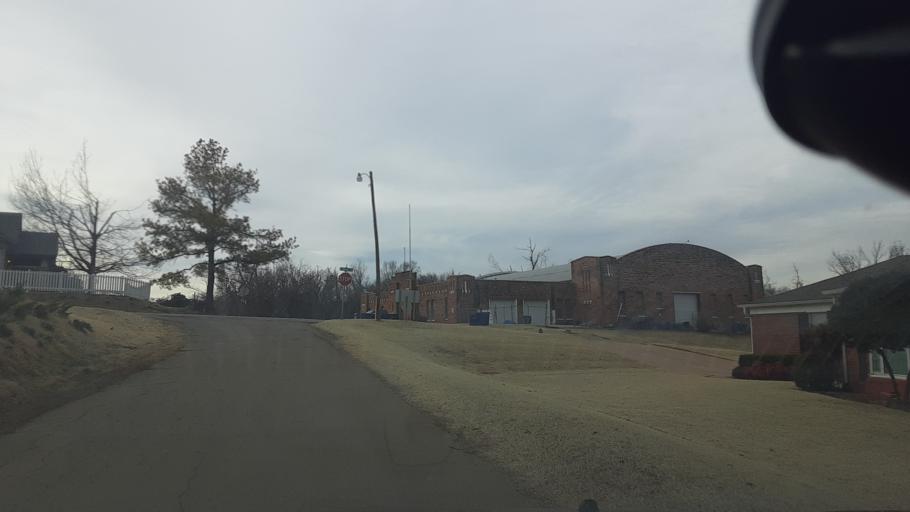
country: US
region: Oklahoma
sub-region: Logan County
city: Guthrie
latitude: 35.8831
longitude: -97.4159
